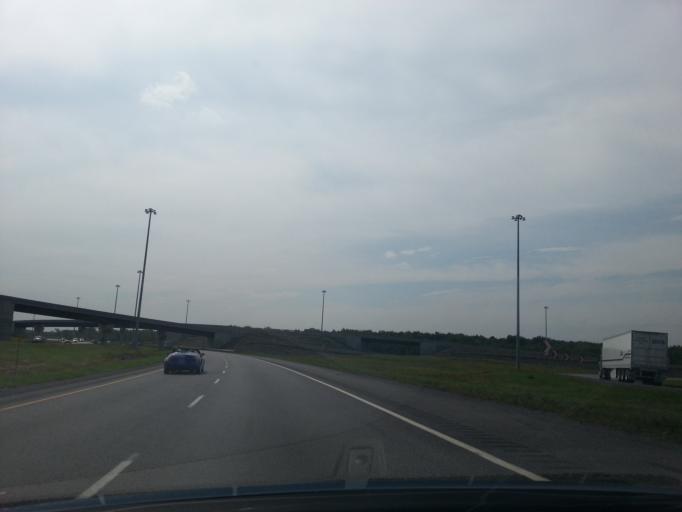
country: CA
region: Quebec
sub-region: Monteregie
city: Saint-Constant
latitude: 45.3693
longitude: -73.6192
